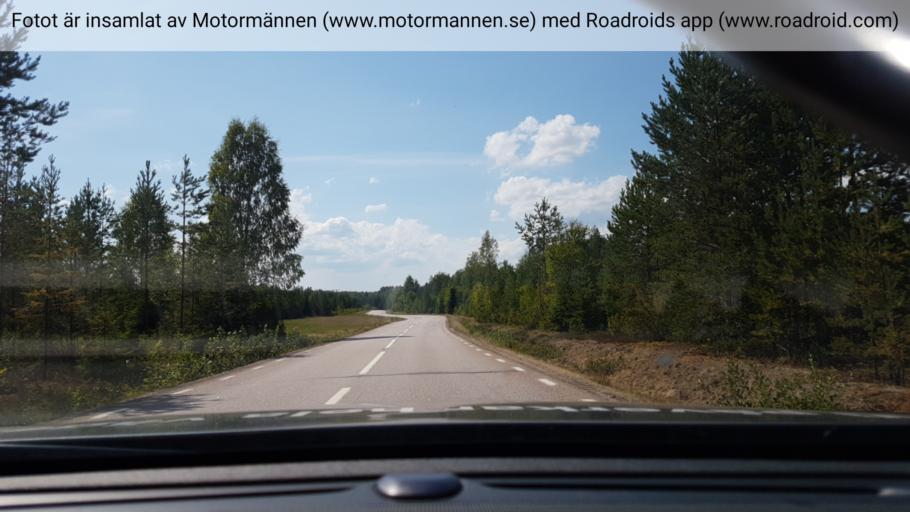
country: SE
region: Gaevleborg
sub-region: Sandvikens Kommun
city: Jarbo
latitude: 60.6545
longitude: 16.4730
